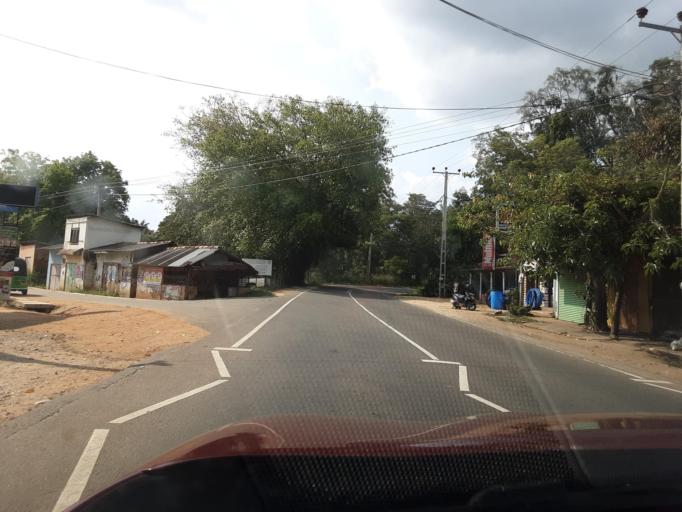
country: LK
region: Uva
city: Haputale
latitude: 6.5233
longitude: 81.1241
